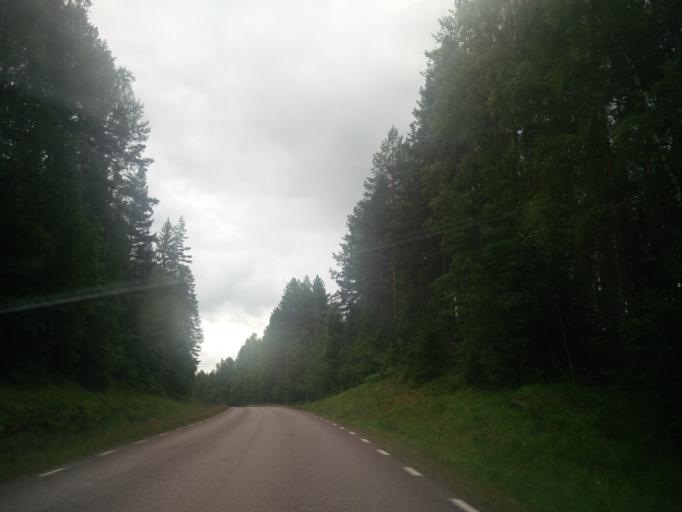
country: SE
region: Vaermland
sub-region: Arvika Kommun
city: Arvika
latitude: 59.9226
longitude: 12.6544
